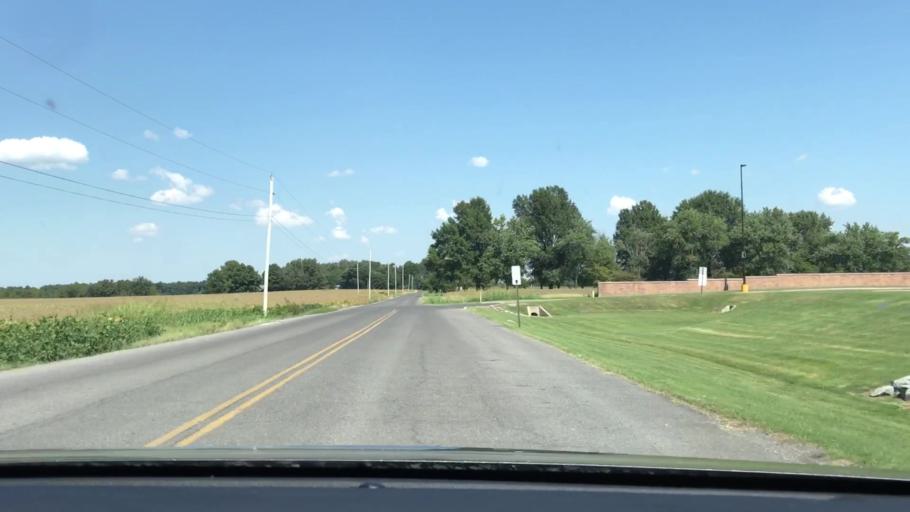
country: US
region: Kentucky
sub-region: Fulton County
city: Fulton
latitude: 36.5172
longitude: -88.9014
